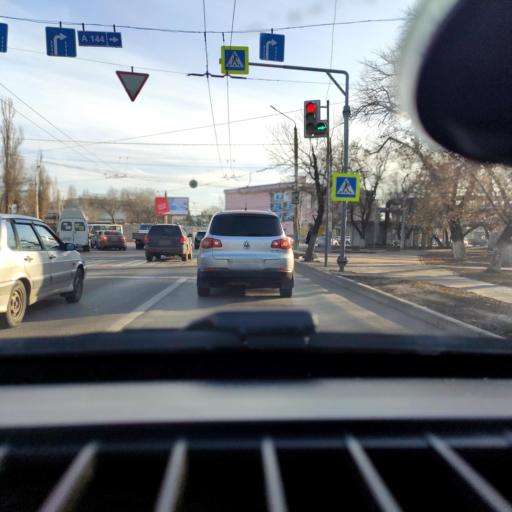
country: RU
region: Voronezj
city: Voronezh
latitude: 51.6312
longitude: 39.2303
